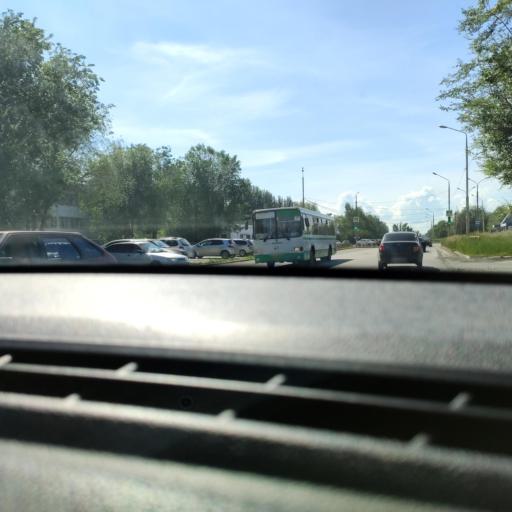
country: RU
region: Samara
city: Podstepki
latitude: 53.5842
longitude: 49.2273
